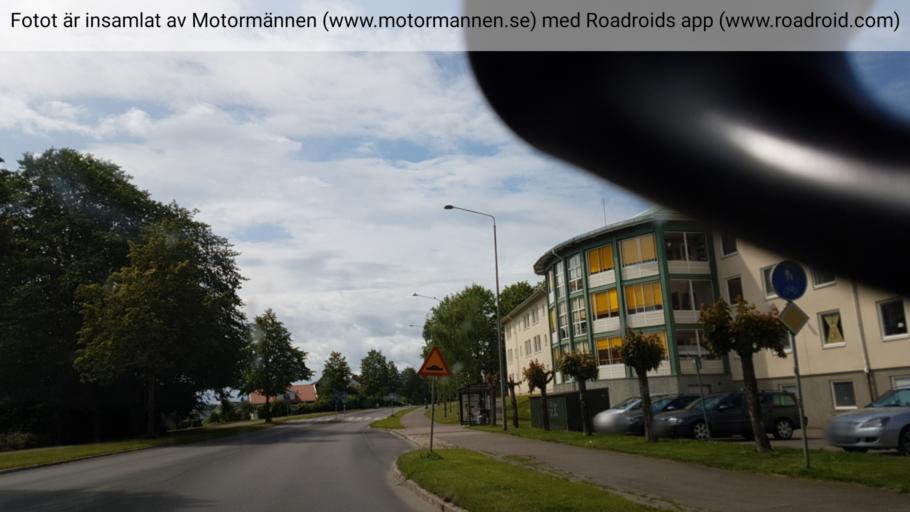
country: SE
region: Vaestra Goetaland
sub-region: Falkopings Kommun
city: Falkoeping
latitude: 58.1845
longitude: 13.5540
